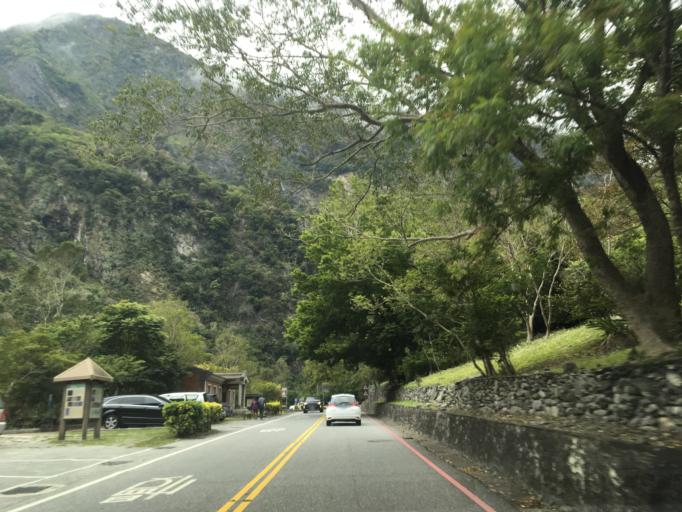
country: TW
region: Taiwan
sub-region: Hualien
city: Hualian
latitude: 24.1794
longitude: 121.5087
